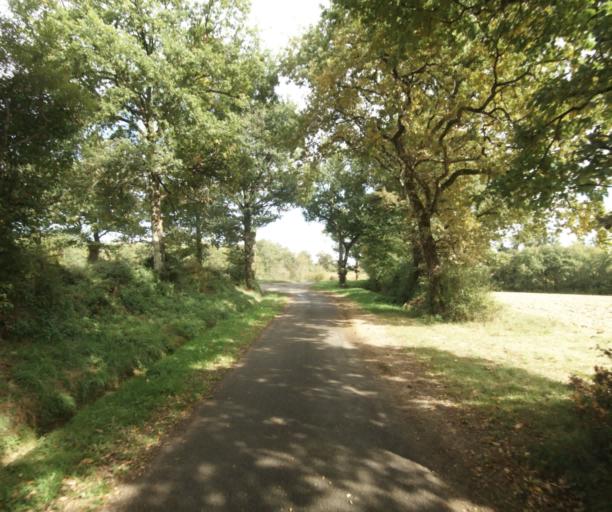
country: FR
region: Midi-Pyrenees
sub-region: Departement du Gers
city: Cazaubon
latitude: 43.8883
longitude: -0.1259
